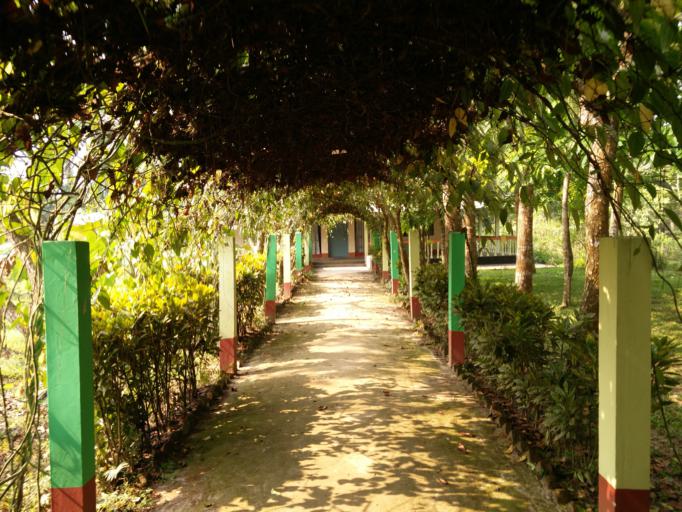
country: BD
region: Dhaka
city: Sherpur
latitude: 24.9174
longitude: 90.1577
